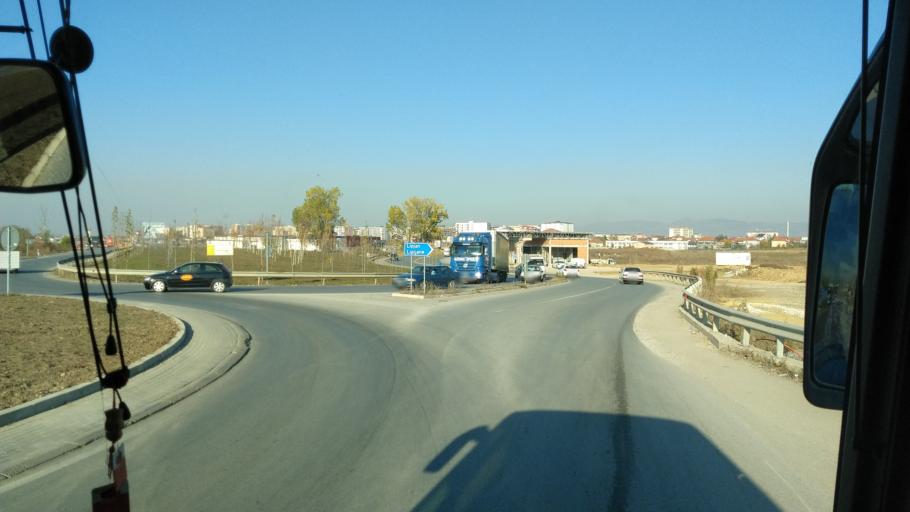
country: XK
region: Pristina
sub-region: Lipjan
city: Lipljan
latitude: 42.5110
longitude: 21.1128
